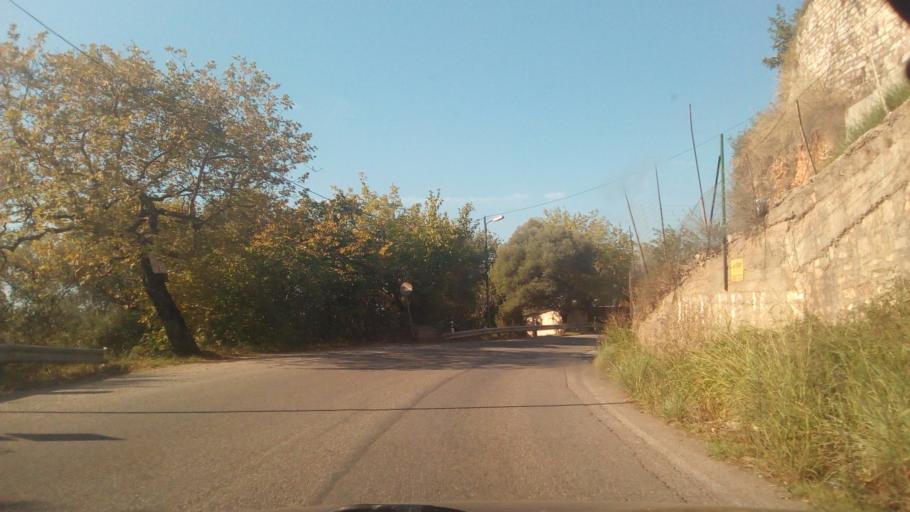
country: GR
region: West Greece
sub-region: Nomos Aitolias kai Akarnanias
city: Nafpaktos
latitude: 38.4110
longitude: 21.8716
